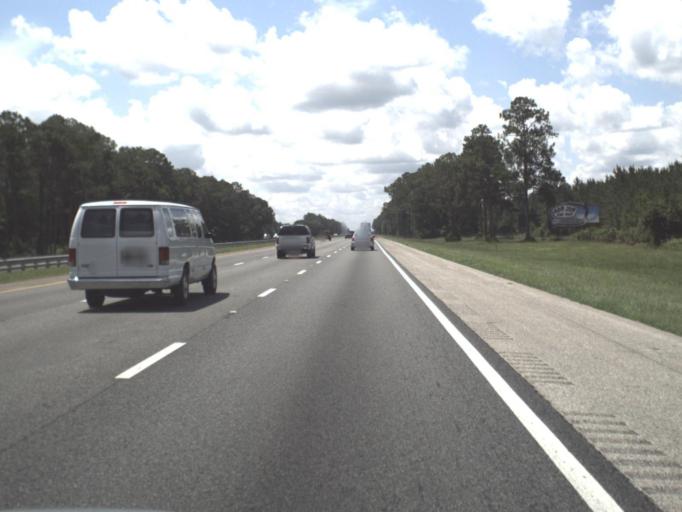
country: US
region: Florida
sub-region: Saint Johns County
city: Saint Augustine Shores
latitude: 29.7863
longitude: -81.3621
